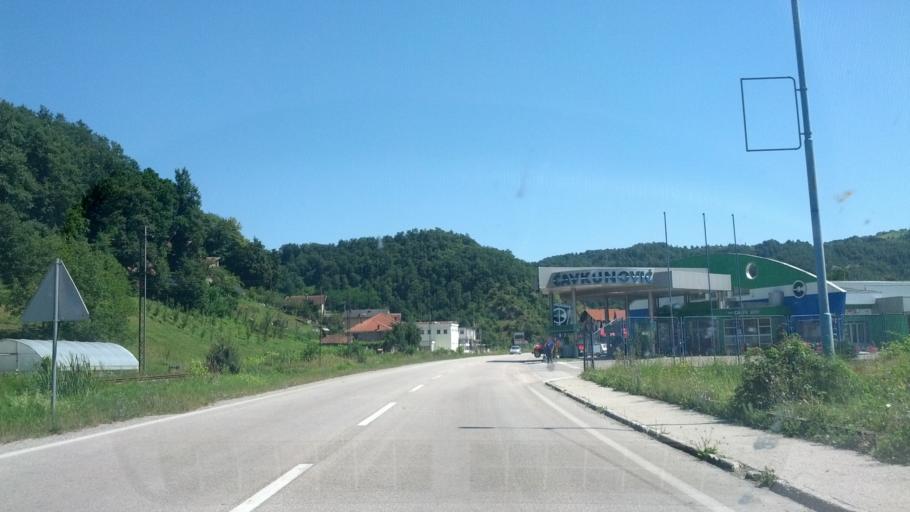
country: BA
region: Federation of Bosnia and Herzegovina
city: Bosanska Krupa
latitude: 44.8966
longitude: 16.1558
